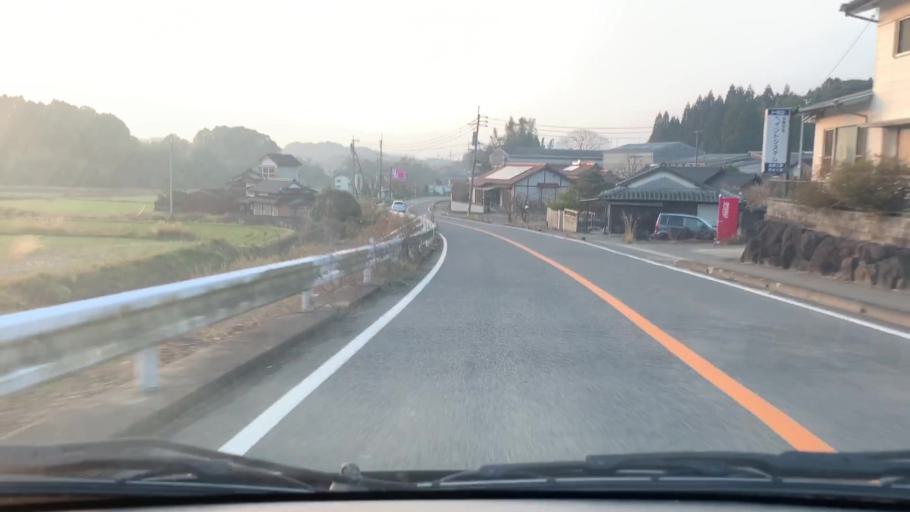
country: JP
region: Saga Prefecture
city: Imaricho-ko
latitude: 33.2651
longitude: 129.9056
